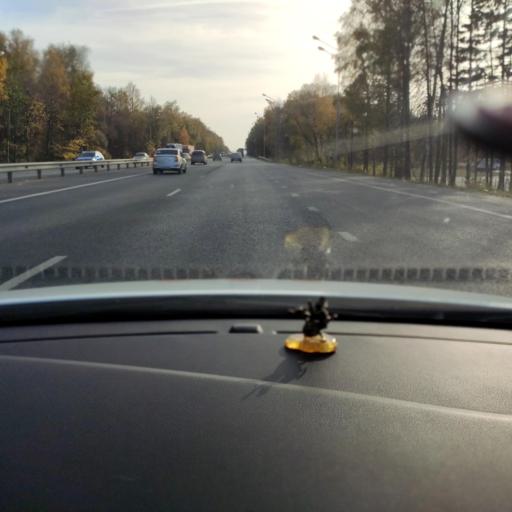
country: RU
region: Tatarstan
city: Osinovo
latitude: 55.8468
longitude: 48.8525
